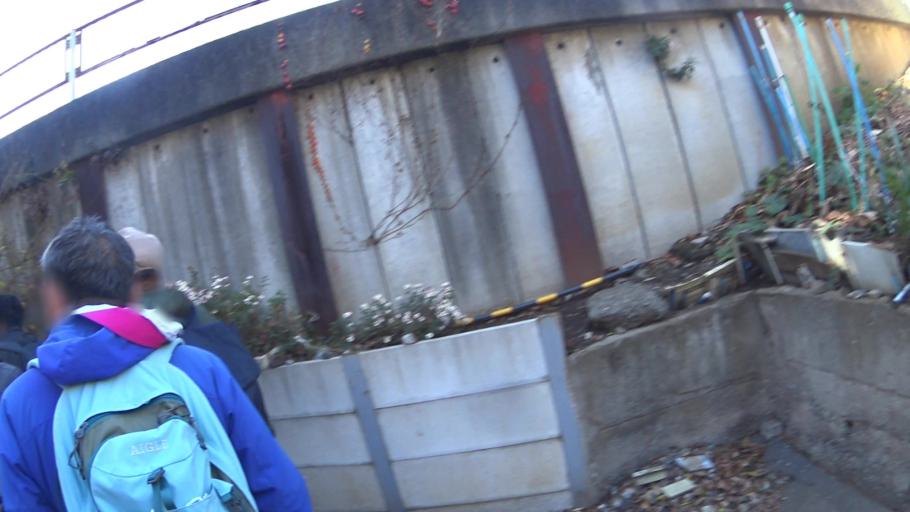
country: JP
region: Saitama
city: Yono
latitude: 35.8562
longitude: 139.6507
